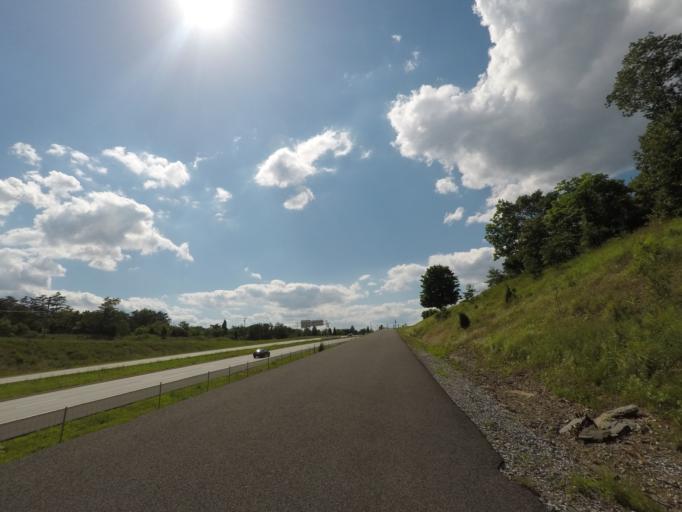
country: US
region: West Virginia
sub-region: Berkeley County
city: Martinsburg
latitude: 39.4285
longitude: -77.9442
